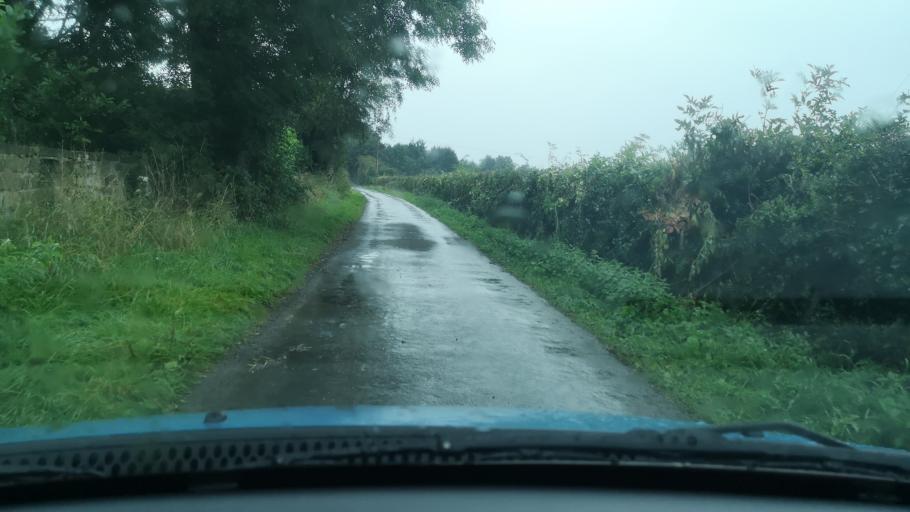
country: GB
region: England
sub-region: City and Borough of Wakefield
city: Low Ackworth
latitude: 53.6650
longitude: -1.3103
